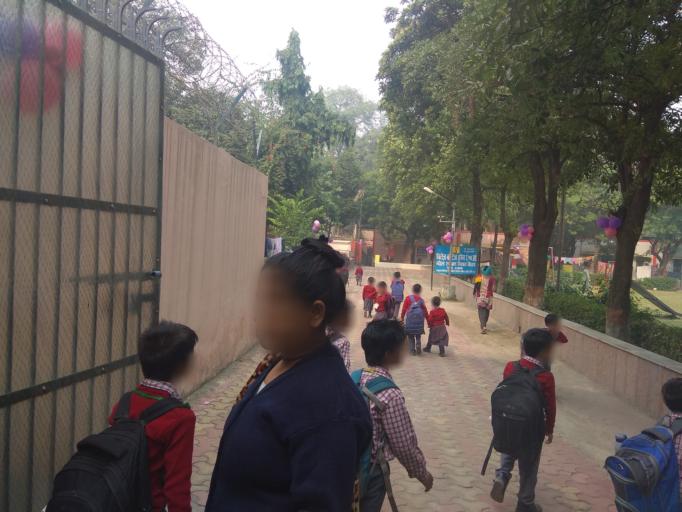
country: IN
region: NCT
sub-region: New Delhi
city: New Delhi
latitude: 28.5720
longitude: 77.2455
